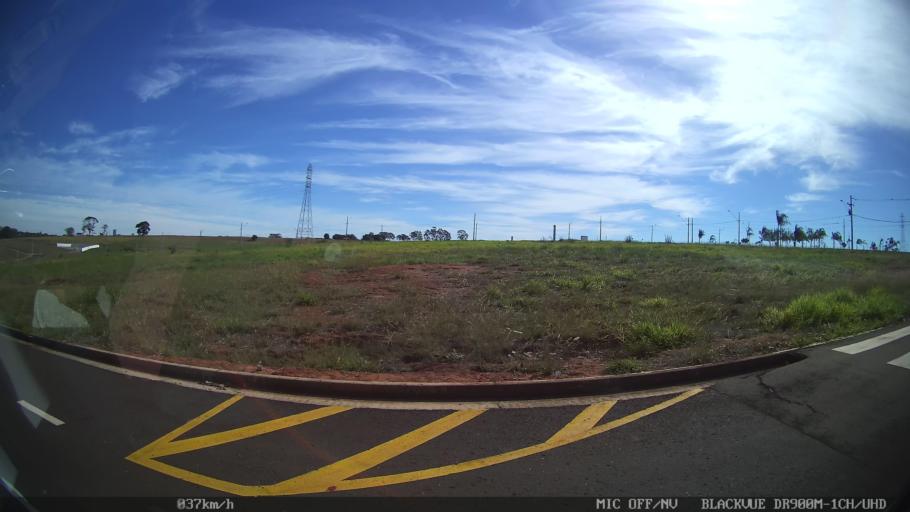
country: BR
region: Sao Paulo
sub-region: Sao Jose Do Rio Preto
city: Sao Jose do Rio Preto
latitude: -20.8545
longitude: -49.3758
